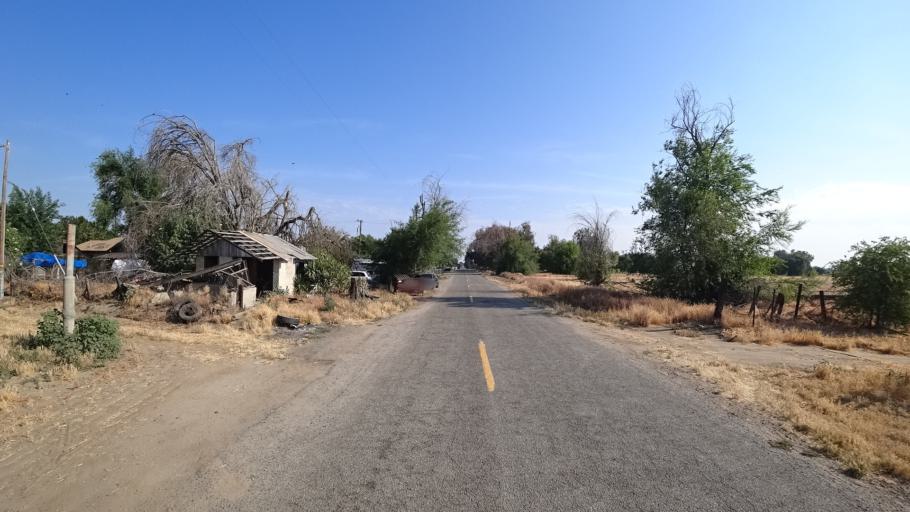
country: US
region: California
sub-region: Kings County
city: Lemoore
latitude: 36.3621
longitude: -119.8161
